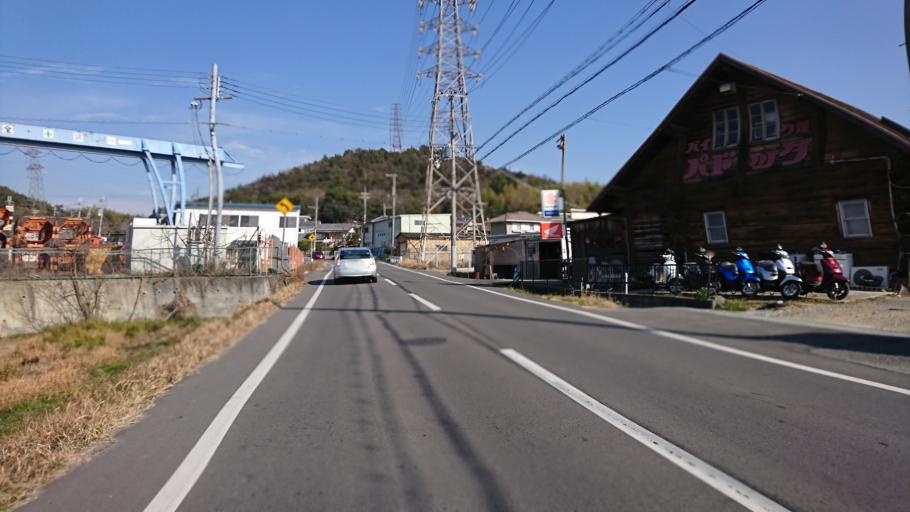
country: JP
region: Hyogo
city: Kakogawacho-honmachi
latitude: 34.7945
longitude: 134.8387
